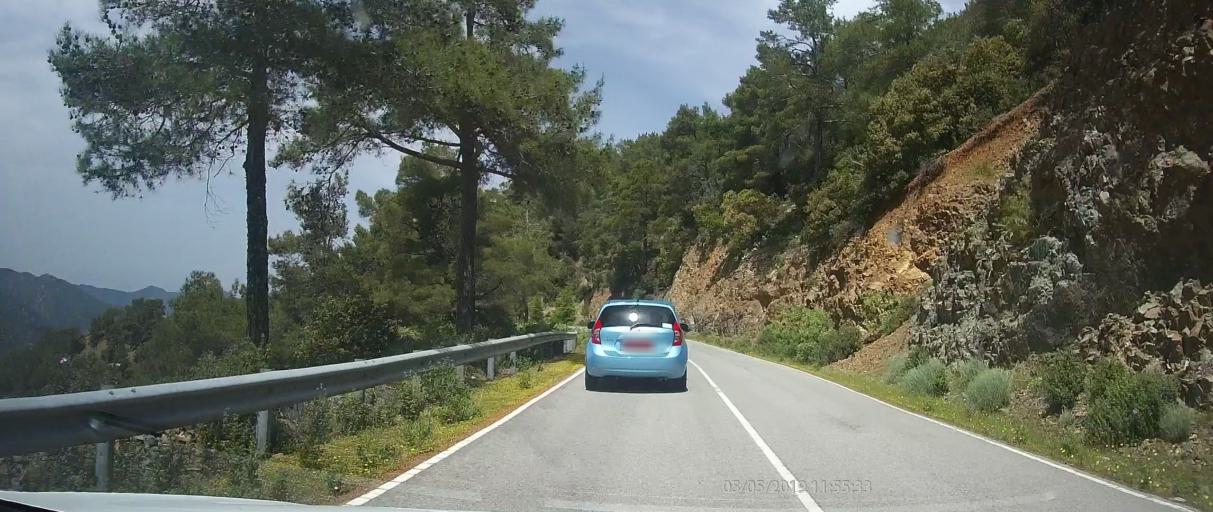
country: CY
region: Lefkosia
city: Lefka
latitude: 35.0090
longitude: 32.7282
